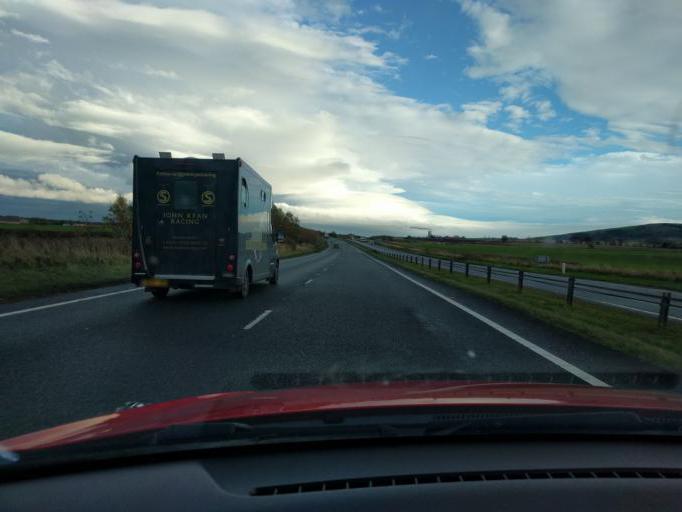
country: GB
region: Scotland
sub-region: East Lothian
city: Dunbar
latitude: 55.9880
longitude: -2.5450
